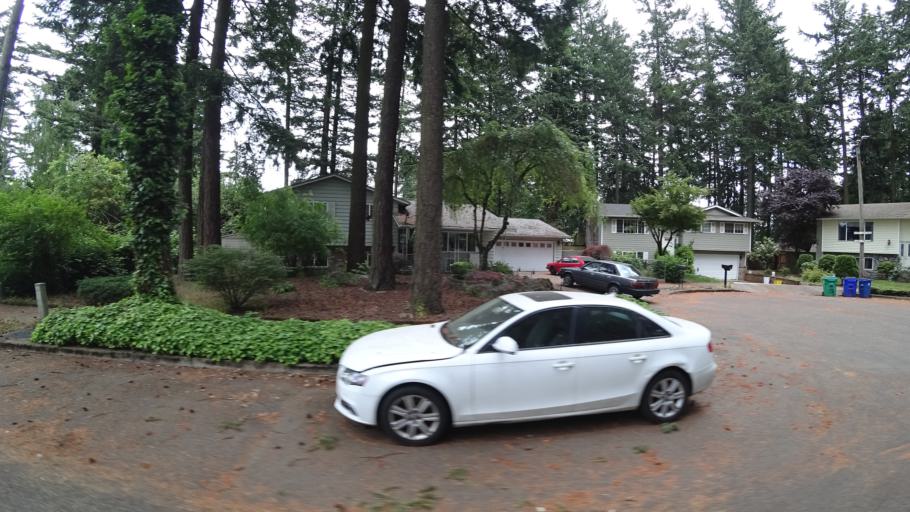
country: US
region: Oregon
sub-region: Clackamas County
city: Happy Valley
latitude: 45.5006
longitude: -122.5050
